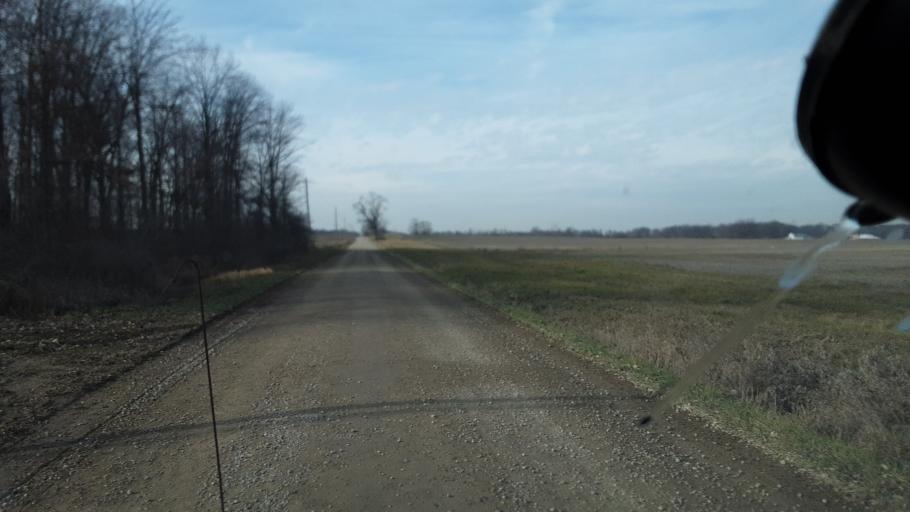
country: US
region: Indiana
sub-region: Allen County
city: Harlan
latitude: 41.2698
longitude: -84.8590
